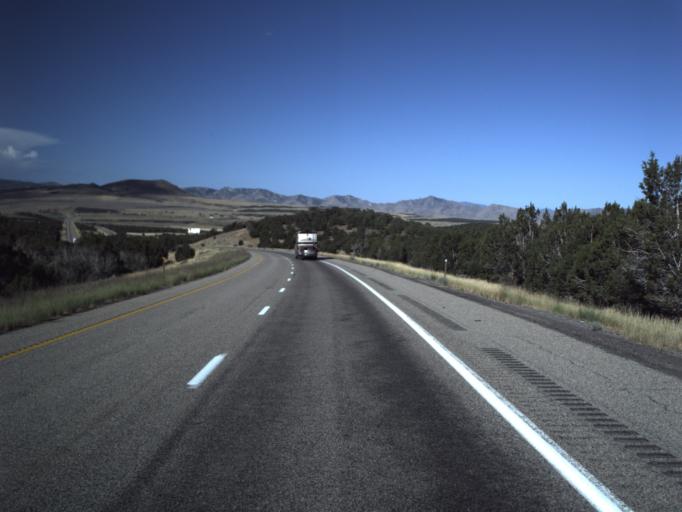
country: US
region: Utah
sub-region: Beaver County
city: Beaver
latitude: 38.6048
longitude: -112.5485
